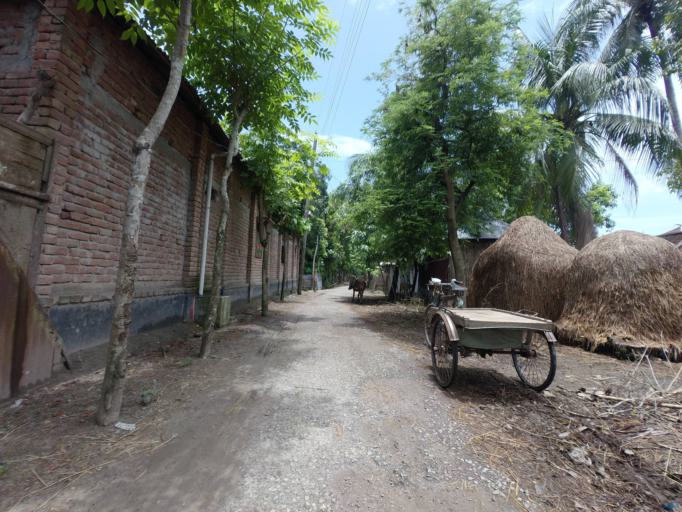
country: BD
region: Khulna
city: Kalia
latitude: 23.0472
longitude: 89.6462
